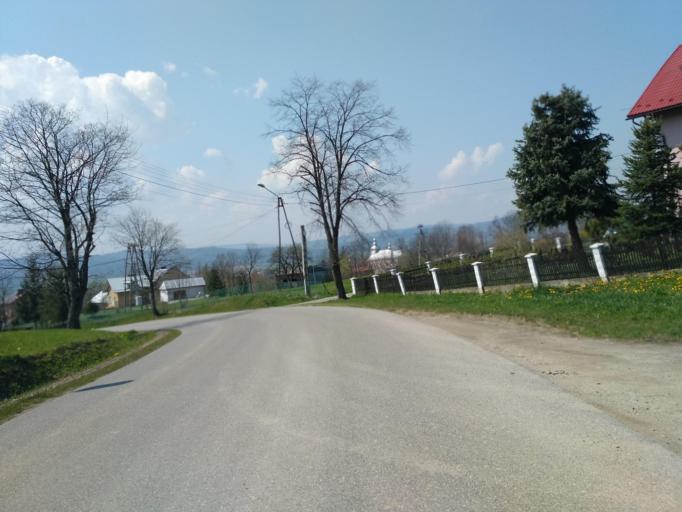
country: PL
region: Subcarpathian Voivodeship
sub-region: Powiat sanocki
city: Zarszyn
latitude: 49.5498
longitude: 21.9844
